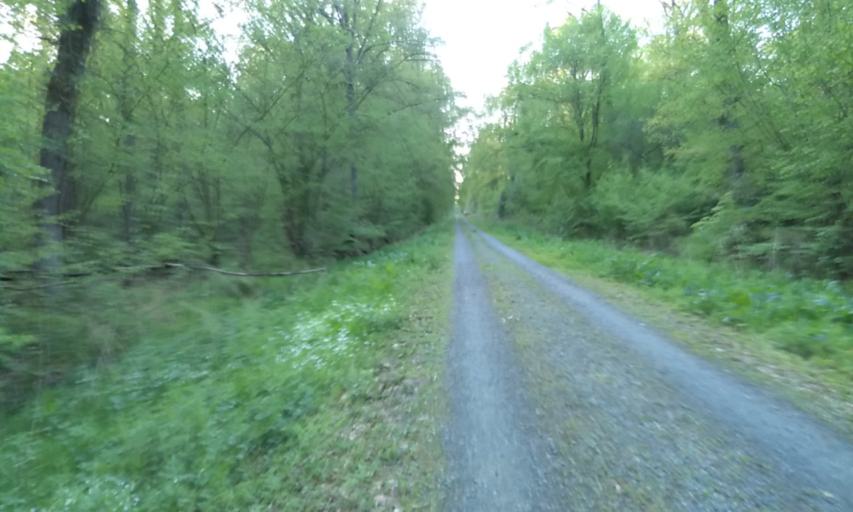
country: DE
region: Lower Saxony
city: Harsefeld
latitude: 53.4184
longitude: 9.5009
